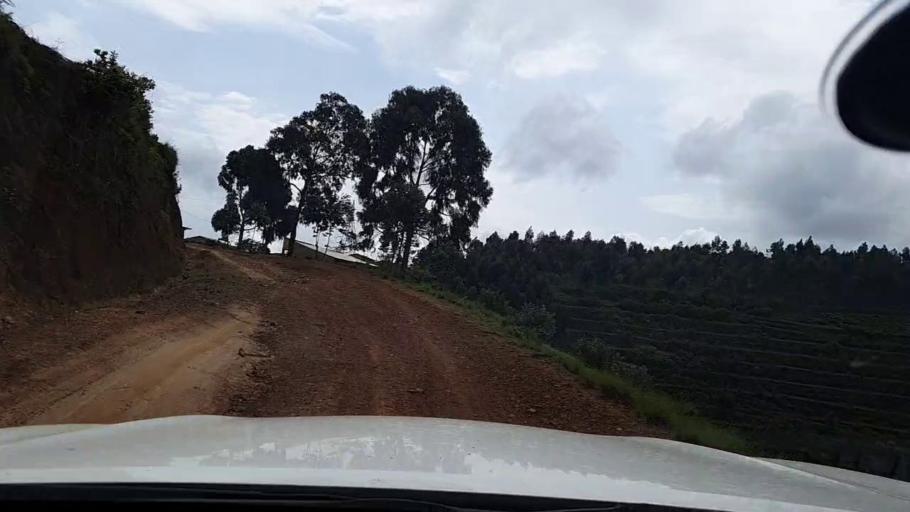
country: RW
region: Western Province
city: Kibuye
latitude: -2.1306
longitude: 29.3758
